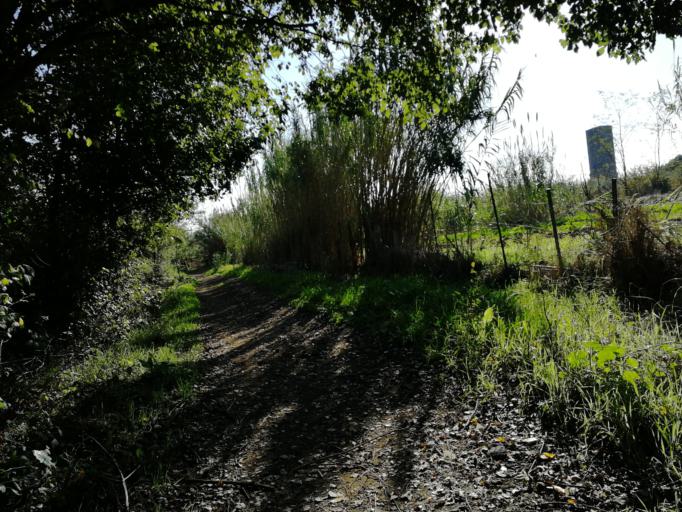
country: IT
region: Latium
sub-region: Citta metropolitana di Roma Capitale
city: Rome
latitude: 41.8577
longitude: 12.5471
